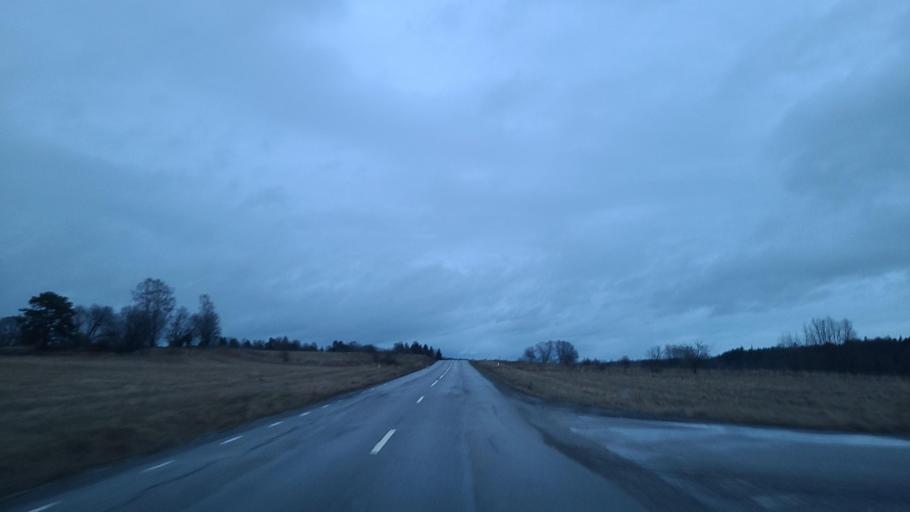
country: SE
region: Stockholm
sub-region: Norrtalje Kommun
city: Norrtalje
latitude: 59.7368
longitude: 18.6277
